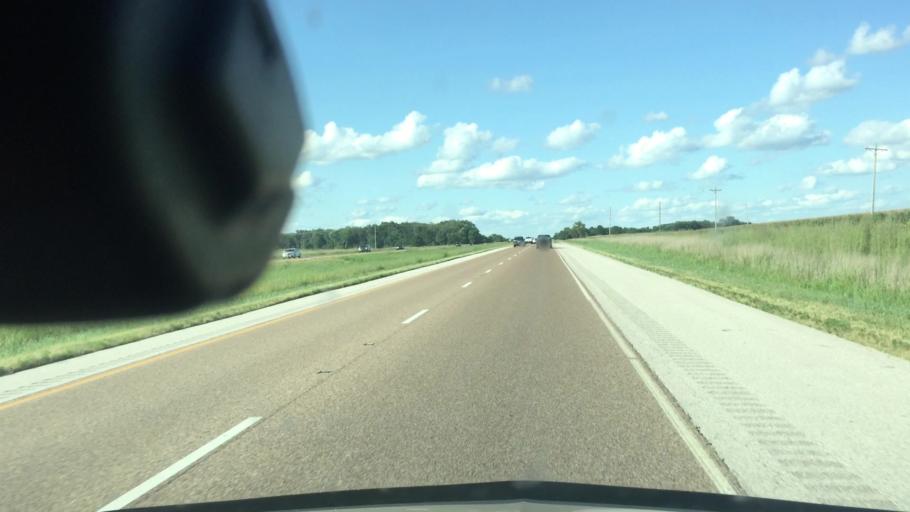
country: US
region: Illinois
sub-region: Macoupin County
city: Mount Olive
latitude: 39.1221
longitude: -89.7184
